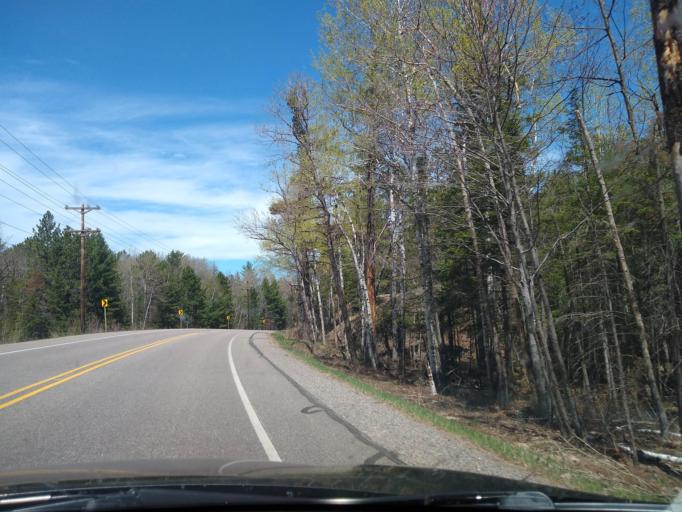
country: US
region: Michigan
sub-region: Marquette County
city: Trowbridge Park
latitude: 46.6114
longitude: -87.4705
